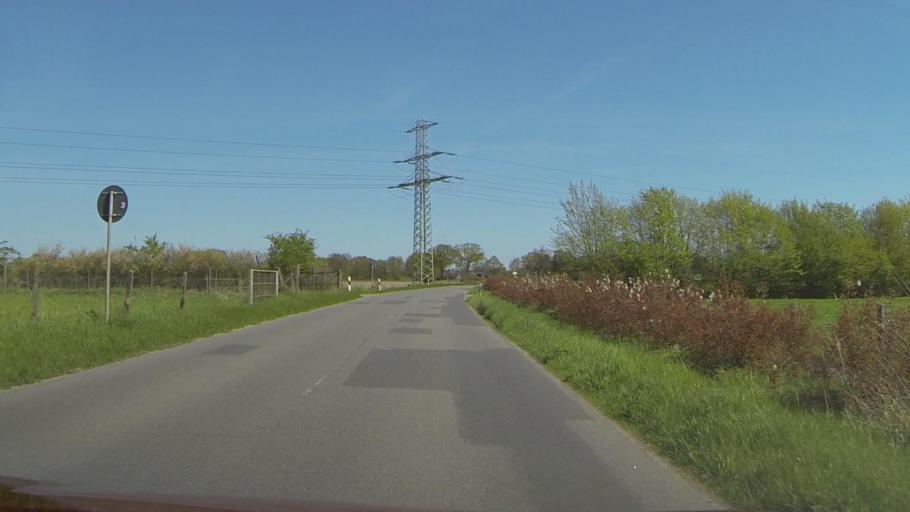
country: DE
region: Schleswig-Holstein
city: Tangstedt
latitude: 53.6616
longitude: 9.8550
